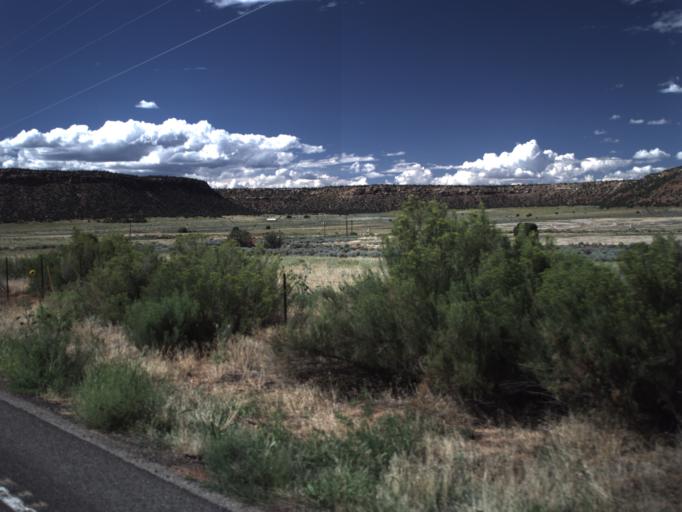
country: US
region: Utah
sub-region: Washington County
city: LaVerkin
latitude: 37.1105
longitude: -113.1464
